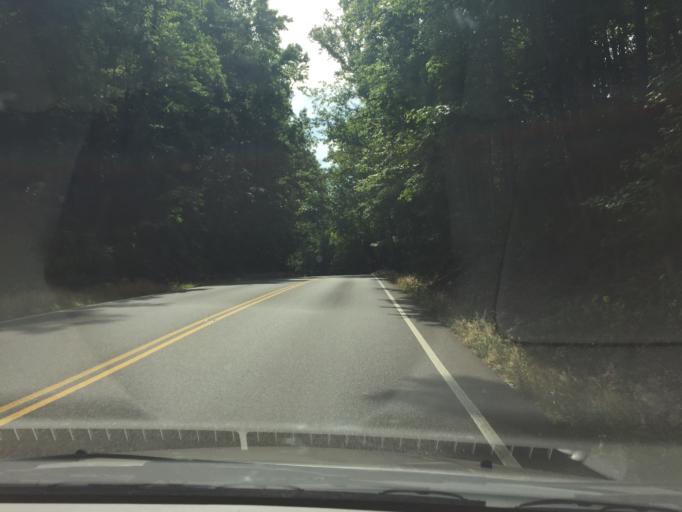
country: US
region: Tennessee
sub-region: Hamilton County
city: Collegedale
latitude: 35.1143
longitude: -84.9726
